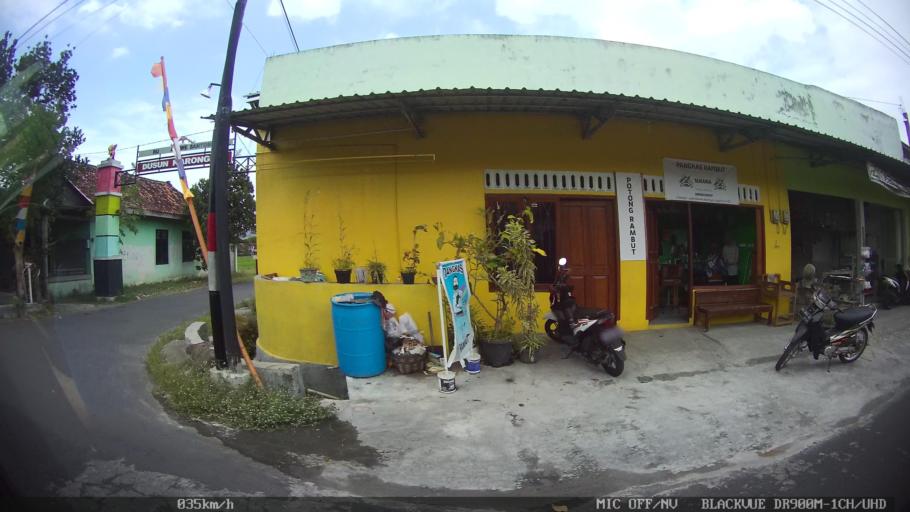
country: ID
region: Daerah Istimewa Yogyakarta
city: Depok
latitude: -7.8129
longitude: 110.4685
